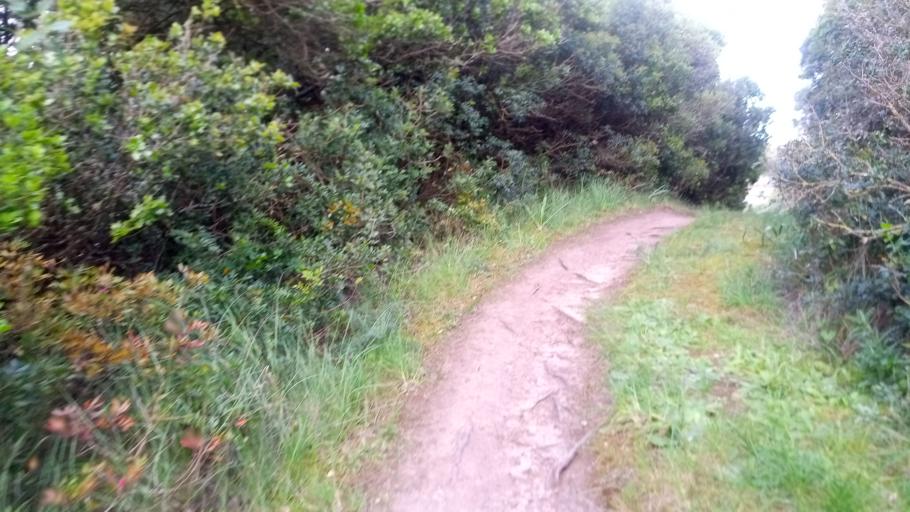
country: PT
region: Leiria
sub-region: Caldas da Rainha
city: Caldas da Rainha
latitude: 39.4015
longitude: -9.1895
